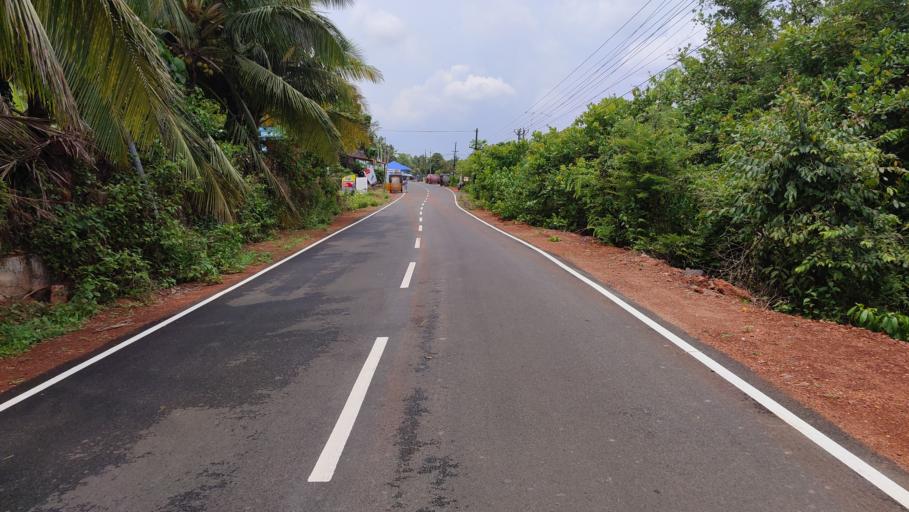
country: IN
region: Kerala
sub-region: Kasaragod District
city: Kannangad
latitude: 12.3160
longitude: 75.1439
